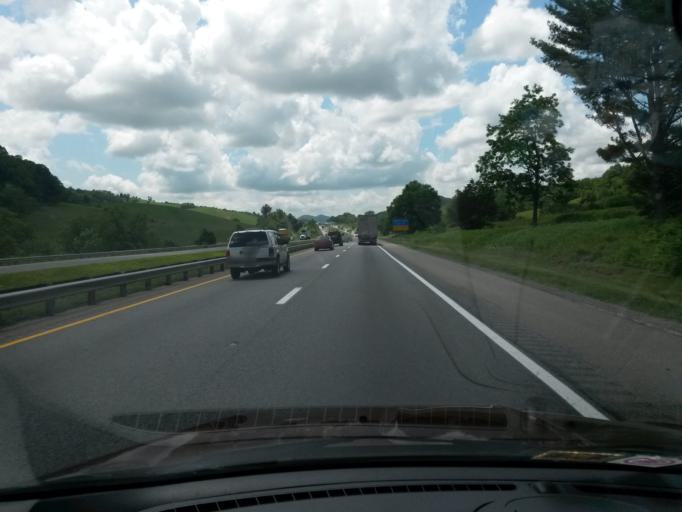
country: US
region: Virginia
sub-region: Pulaski County
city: Pulaski
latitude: 37.0019
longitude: -80.7665
